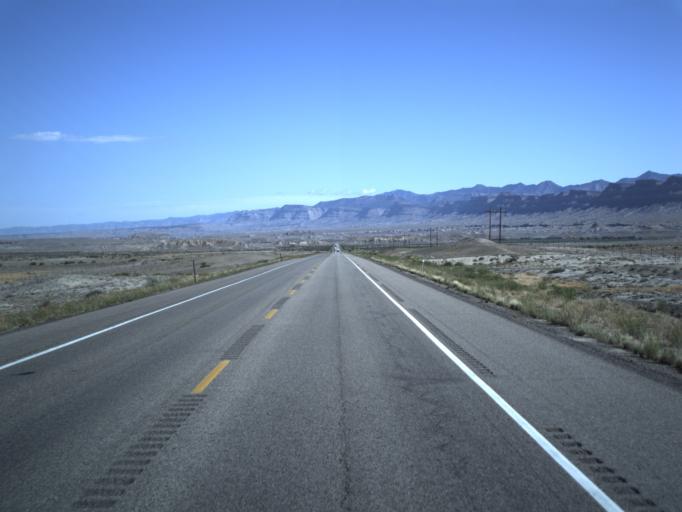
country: US
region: Utah
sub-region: Carbon County
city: East Carbon City
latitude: 39.2216
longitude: -110.3387
